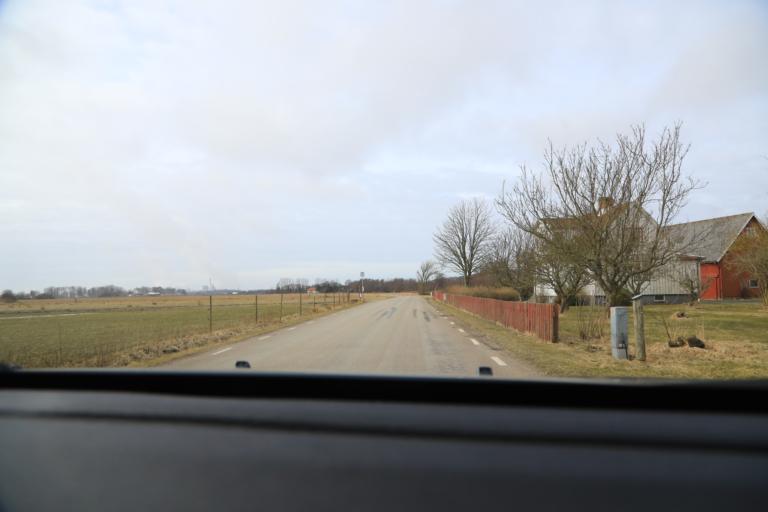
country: SE
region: Halland
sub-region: Varbergs Kommun
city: Veddige
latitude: 57.2286
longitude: 12.2414
